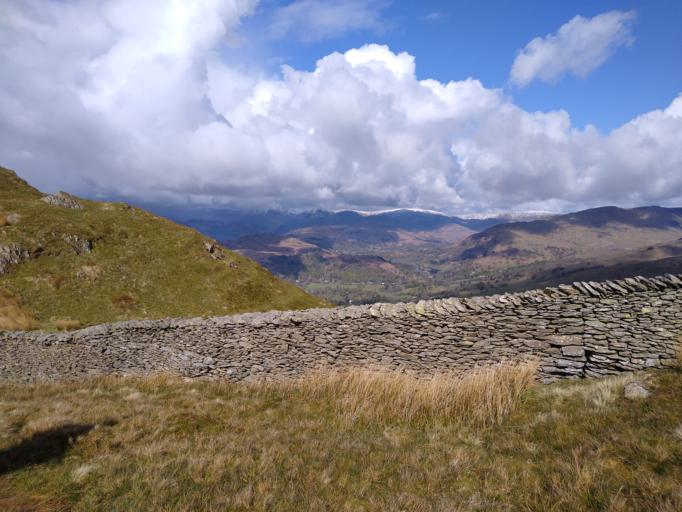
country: GB
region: England
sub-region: Cumbria
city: Ambleside
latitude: 54.4313
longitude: -2.9308
